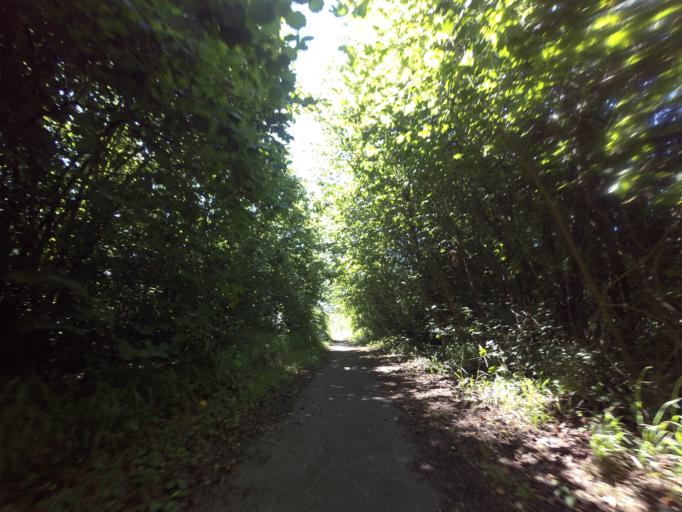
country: GB
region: England
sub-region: Kent
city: Eastry
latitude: 51.2249
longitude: 1.3013
